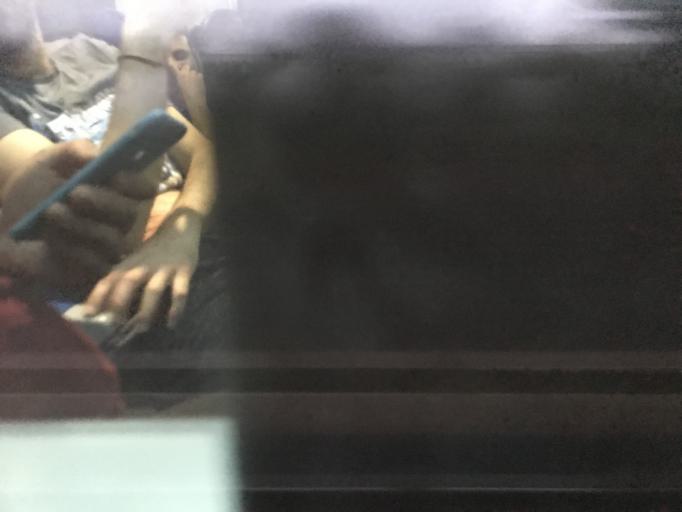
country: TR
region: Kocaeli
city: Derince
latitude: 40.7490
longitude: 29.8016
